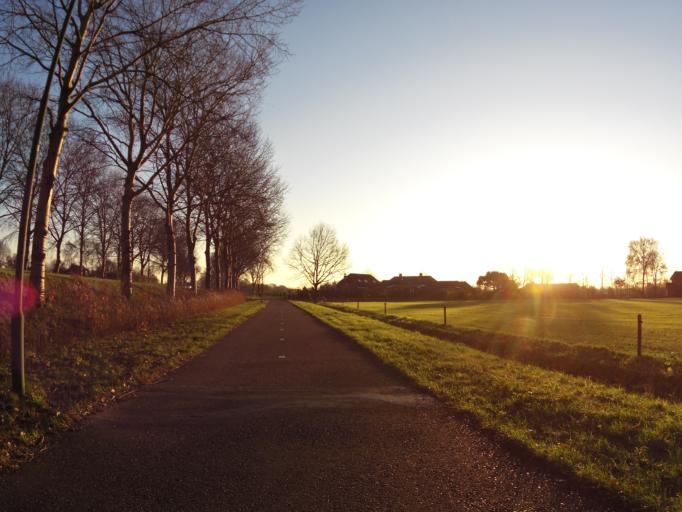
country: NL
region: North Brabant
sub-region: Gemeente Sint-Michielsgestel
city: Sint-Michielsgestel
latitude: 51.6474
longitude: 5.3263
